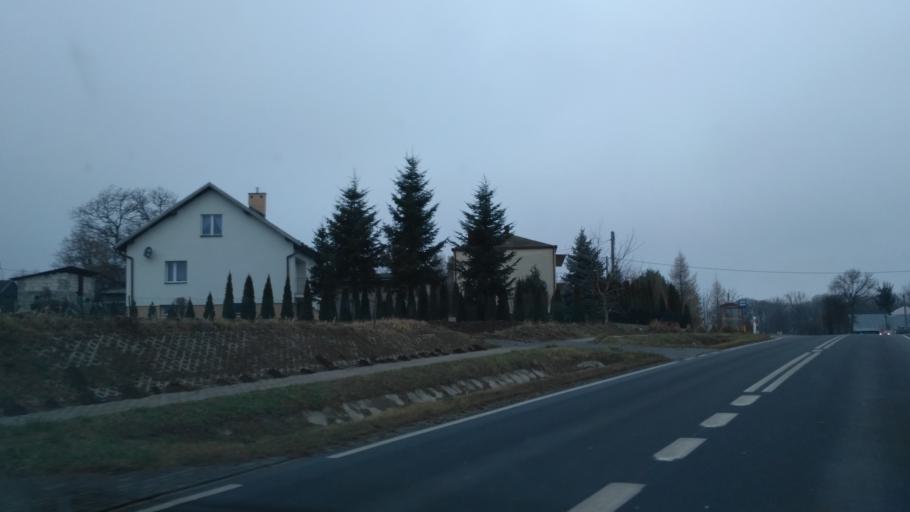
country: PL
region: Subcarpathian Voivodeship
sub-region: Powiat jaroslawski
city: Pruchnik
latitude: 49.9171
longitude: 22.5661
